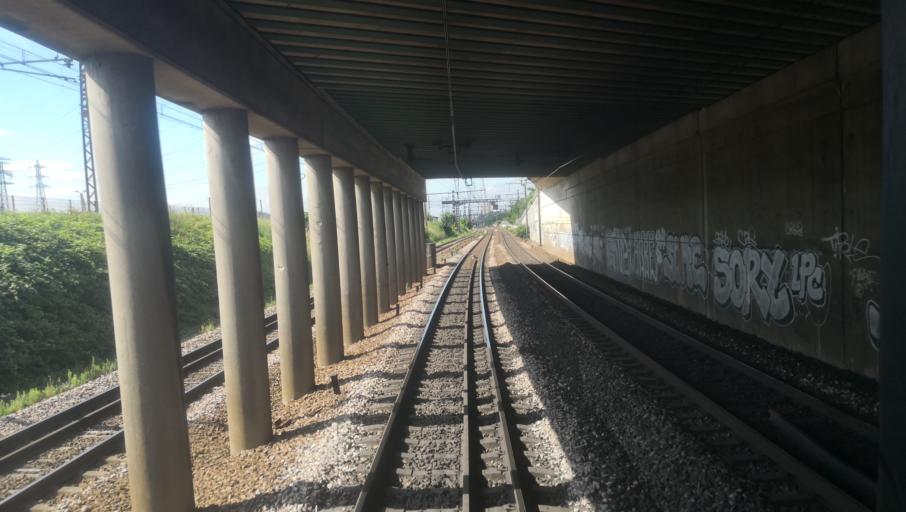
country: FR
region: Ile-de-France
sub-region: Departement du Val-de-Marne
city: Choisy-le-Roi
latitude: 48.7798
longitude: 2.4351
